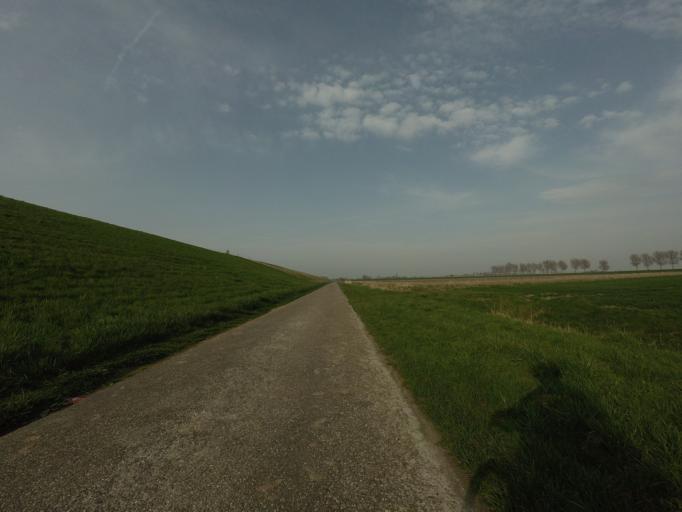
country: NL
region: Zeeland
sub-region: Gemeente Terneuzen
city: Zaamslag
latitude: 51.3814
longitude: 3.9644
